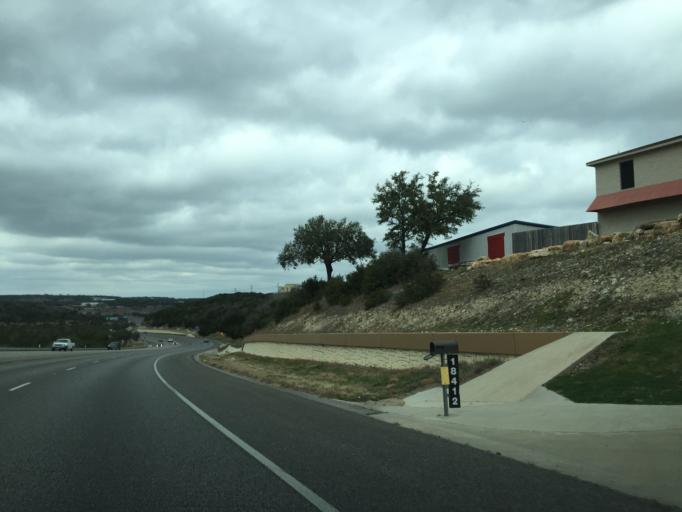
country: US
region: Texas
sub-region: Travis County
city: The Hills
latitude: 30.3334
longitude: -98.0273
